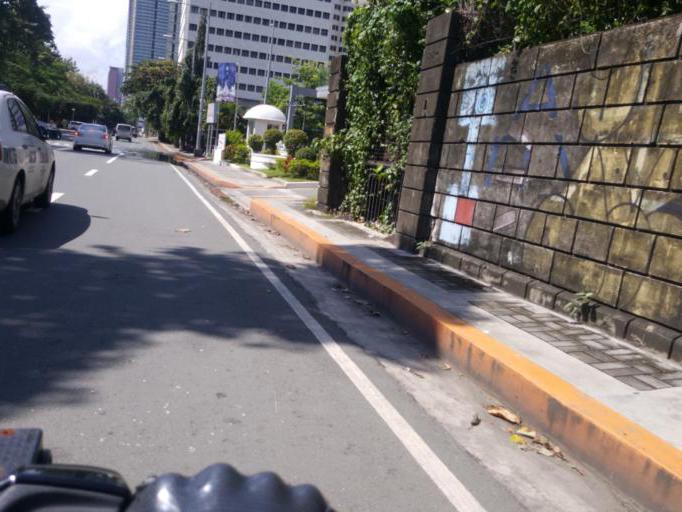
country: PH
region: Metro Manila
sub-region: City of Manila
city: Port Area
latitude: 14.5703
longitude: 120.9827
